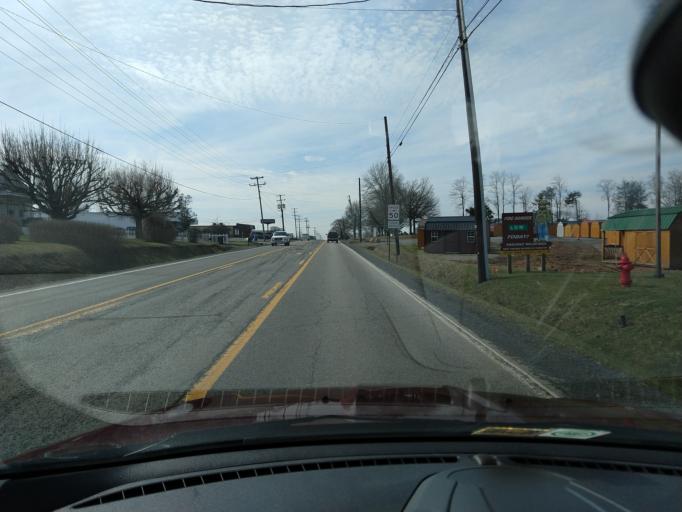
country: US
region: West Virginia
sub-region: Greenbrier County
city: Lewisburg
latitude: 37.8337
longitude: -80.4176
